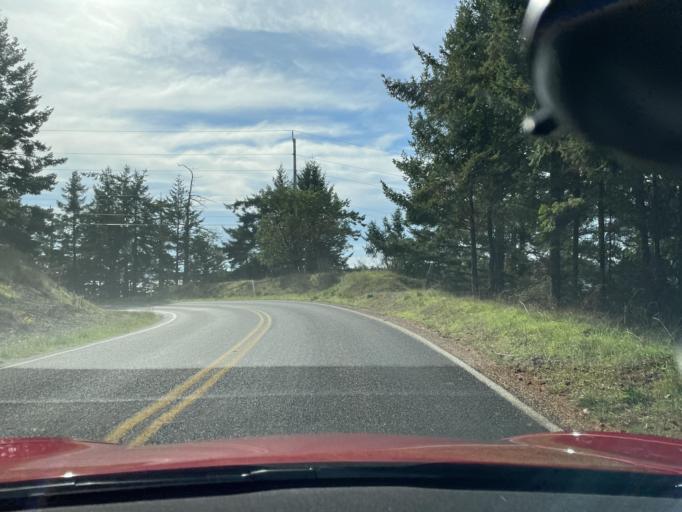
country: US
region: Washington
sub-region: San Juan County
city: Friday Harbor
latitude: 48.5210
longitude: -123.0033
